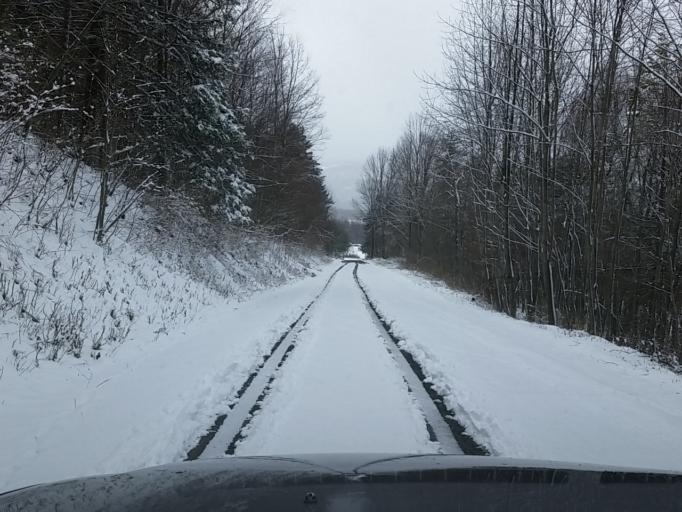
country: US
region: Pennsylvania
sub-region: Sullivan County
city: Laporte
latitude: 41.3589
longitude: -76.4733
